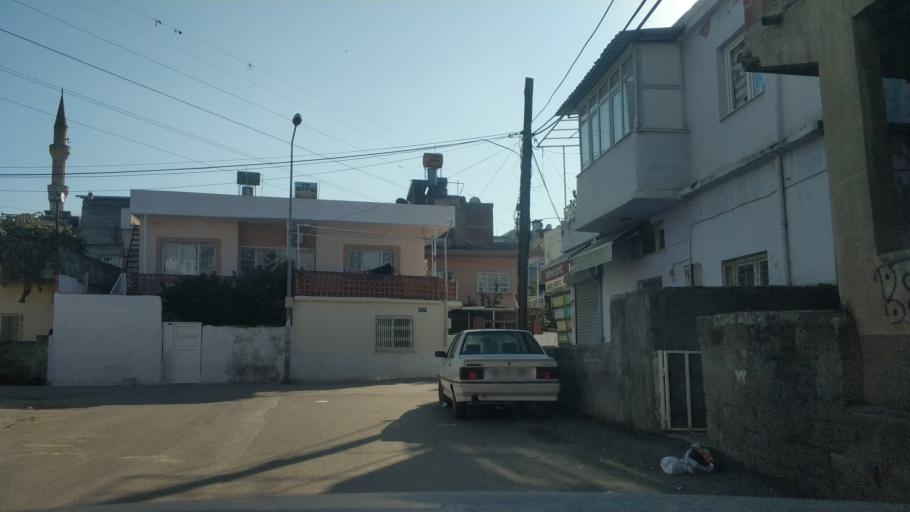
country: TR
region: Adana
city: Adana
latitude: 37.0090
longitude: 35.3121
